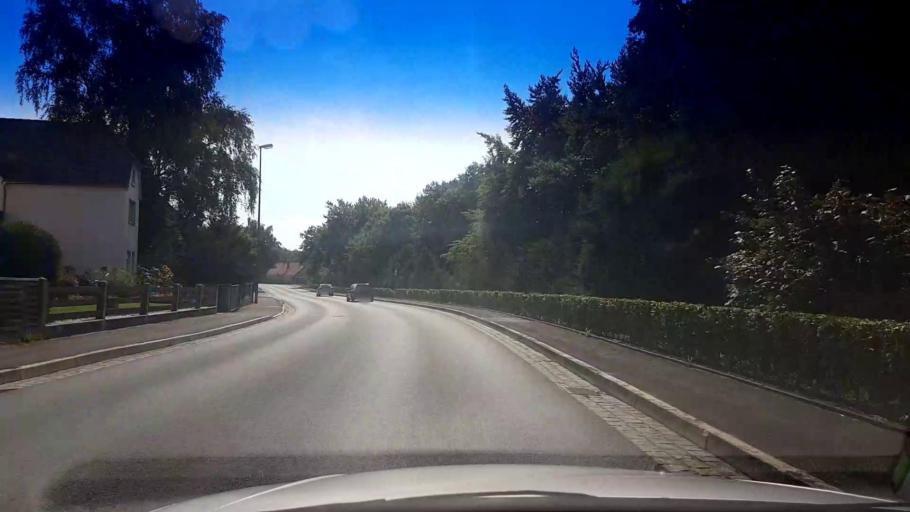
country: DE
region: Bavaria
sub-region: Upper Franconia
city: Eckersdorf
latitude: 49.9343
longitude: 11.5105
